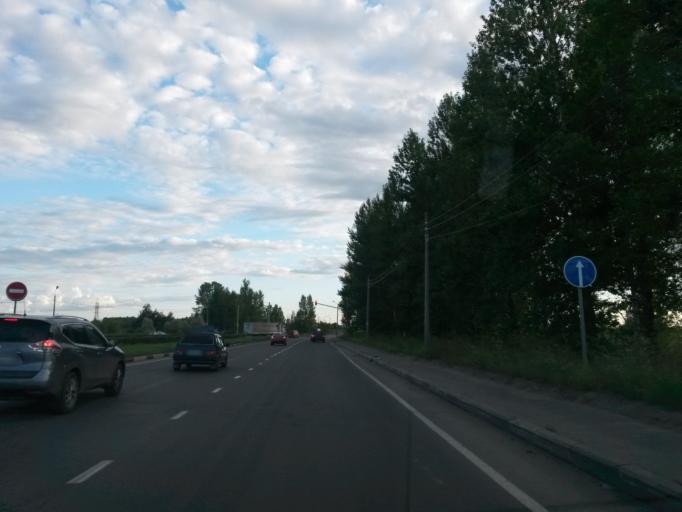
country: RU
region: Jaroslavl
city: Yaroslavl
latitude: 57.6730
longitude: 39.7719
